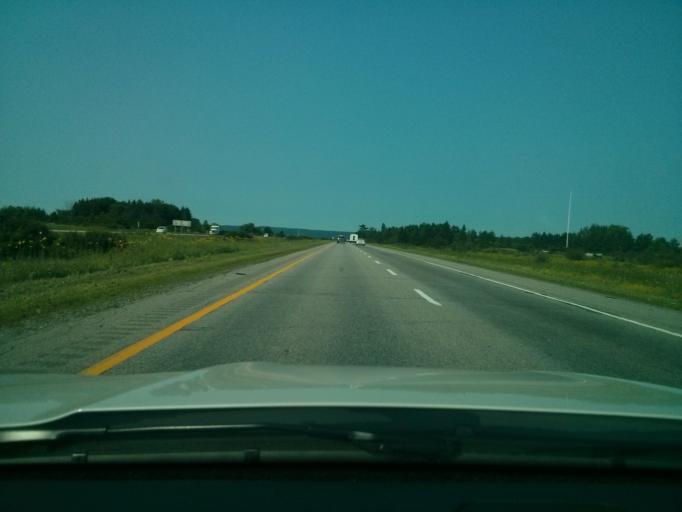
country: CA
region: Quebec
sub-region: Outaouais
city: Gatineau
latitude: 45.5064
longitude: -75.6876
